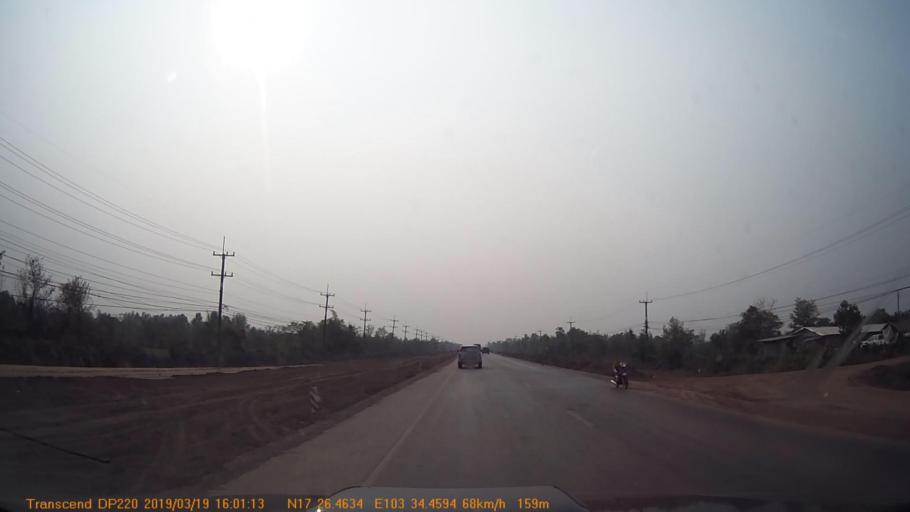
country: TH
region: Sakon Nakhon
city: Sawang Daen Din
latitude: 17.4410
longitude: 103.5738
